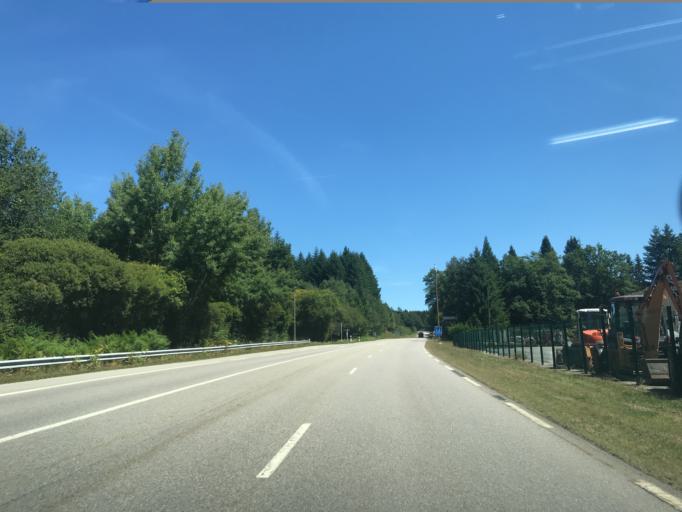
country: FR
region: Limousin
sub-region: Departement de la Correze
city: Meymac
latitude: 45.4770
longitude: 2.1790
